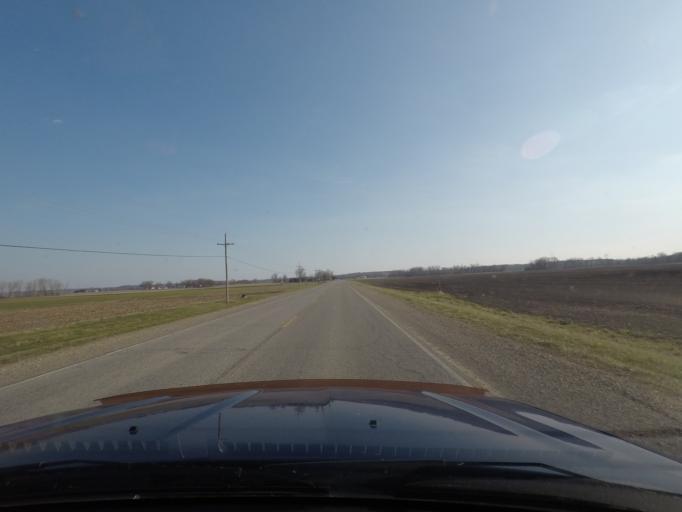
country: US
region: Kansas
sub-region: Jefferson County
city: Oskaloosa
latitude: 39.0691
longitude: -95.3820
